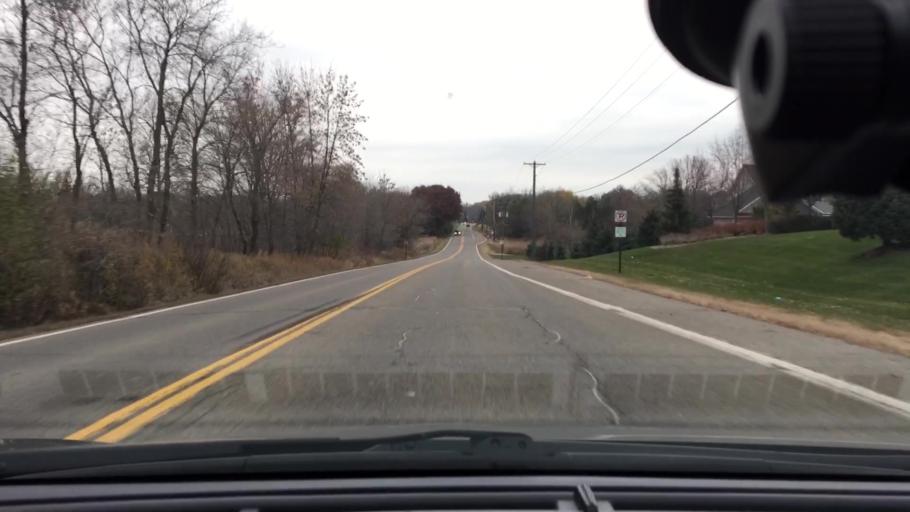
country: US
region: Minnesota
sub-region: Hennepin County
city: Corcoran
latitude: 45.1001
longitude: -93.5122
